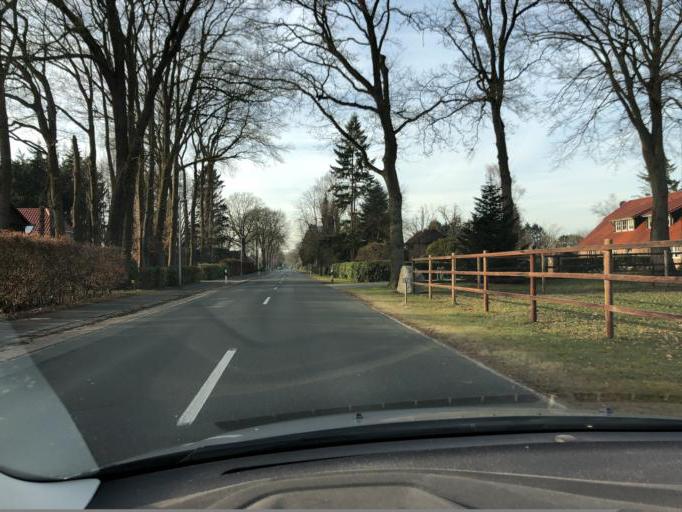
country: DE
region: Lower Saxony
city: Bad Zwischenahn
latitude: 53.1466
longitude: 8.0914
